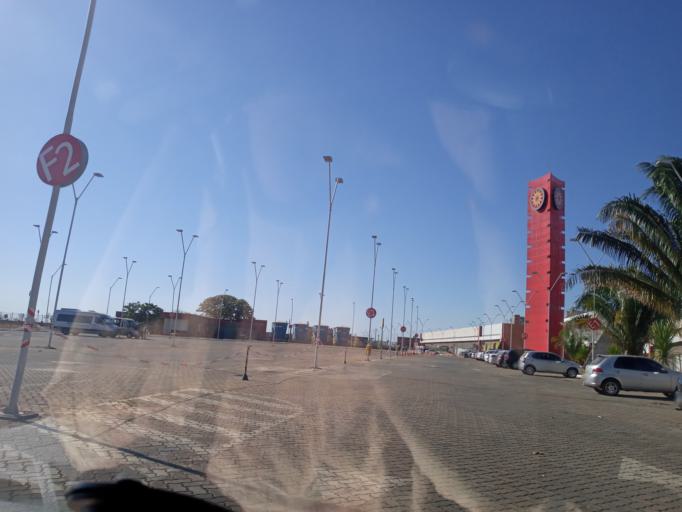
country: BR
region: Goias
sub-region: Abadiania
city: Abadiania
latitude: -16.1227
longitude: -48.3990
